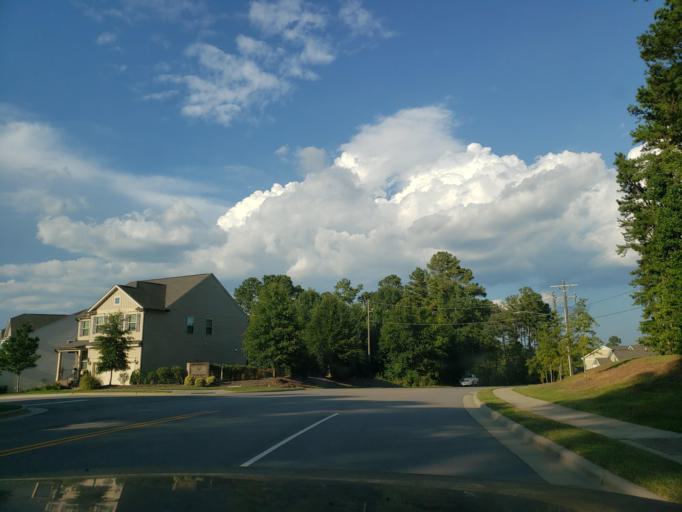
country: US
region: North Carolina
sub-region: Durham County
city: Durham
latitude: 35.9425
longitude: -78.9242
